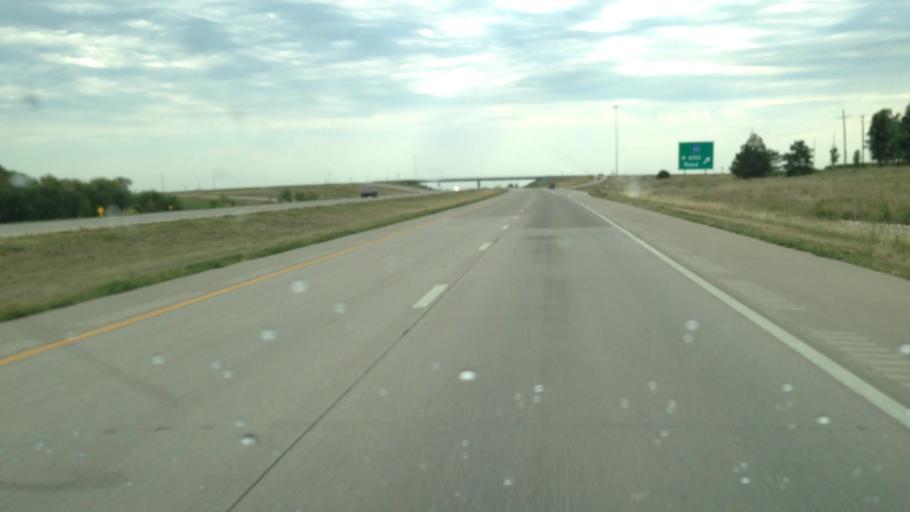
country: US
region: Kansas
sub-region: Douglas County
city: Baldwin City
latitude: 38.8392
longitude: -95.2686
